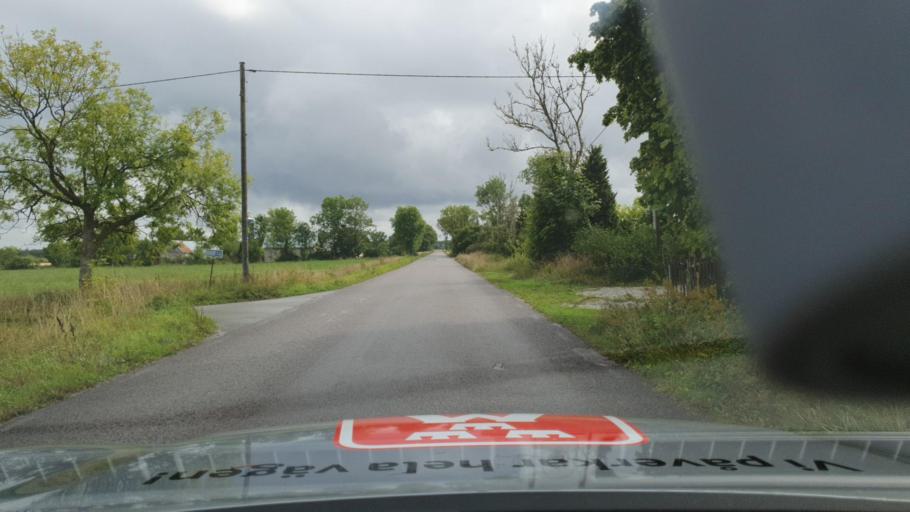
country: SE
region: Gotland
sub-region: Gotland
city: Slite
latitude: 57.6925
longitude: 18.7609
